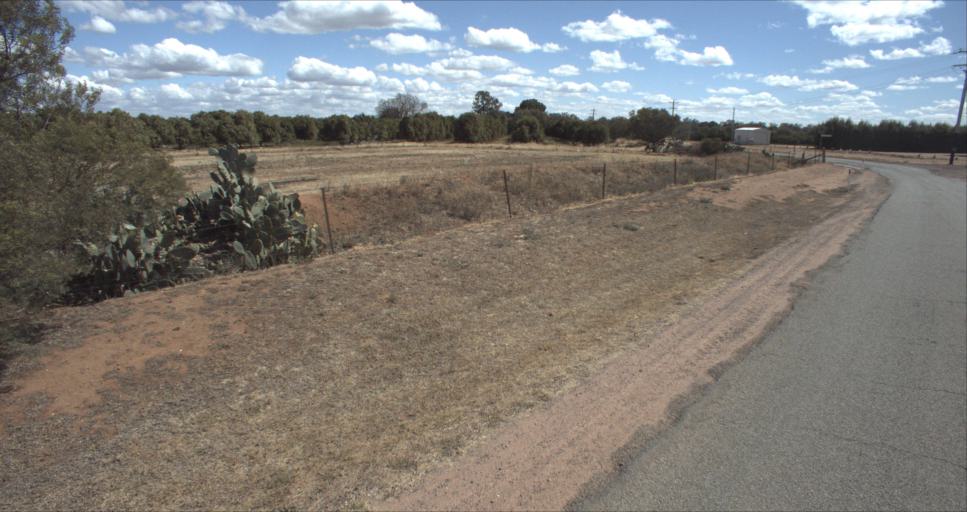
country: AU
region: New South Wales
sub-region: Leeton
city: Leeton
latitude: -34.5126
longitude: 146.2425
